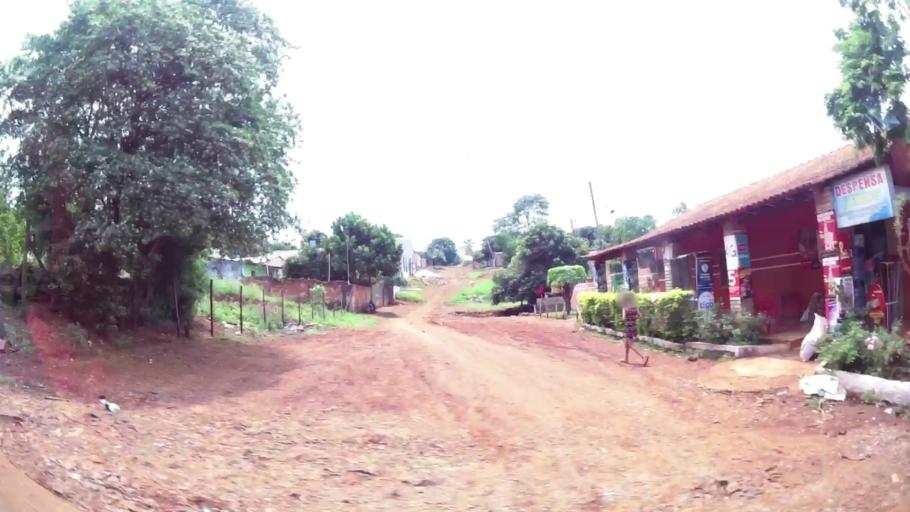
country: PY
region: Alto Parana
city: Ciudad del Este
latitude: -25.5033
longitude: -54.6187
